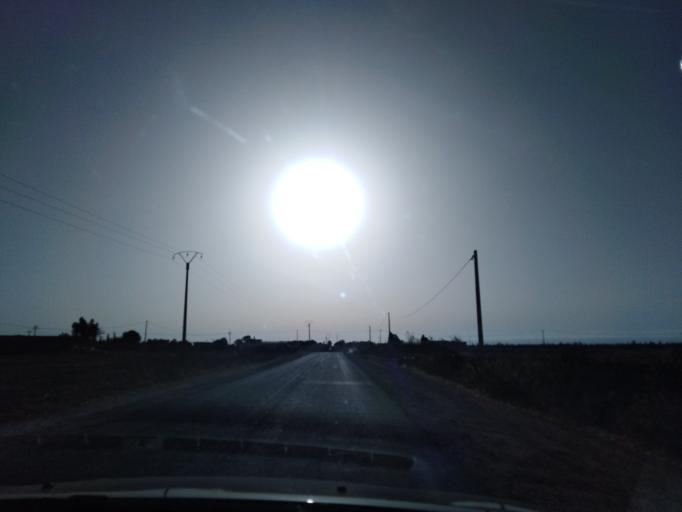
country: MA
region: Doukkala-Abda
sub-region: Safi
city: Safi
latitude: 32.4786
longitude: -8.9009
